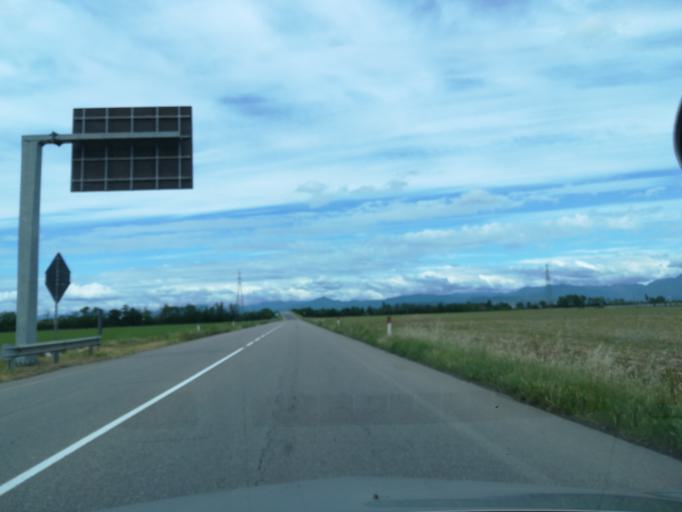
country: IT
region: Lombardy
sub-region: Provincia di Bergamo
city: Calcio
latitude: 45.5271
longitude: 9.8336
